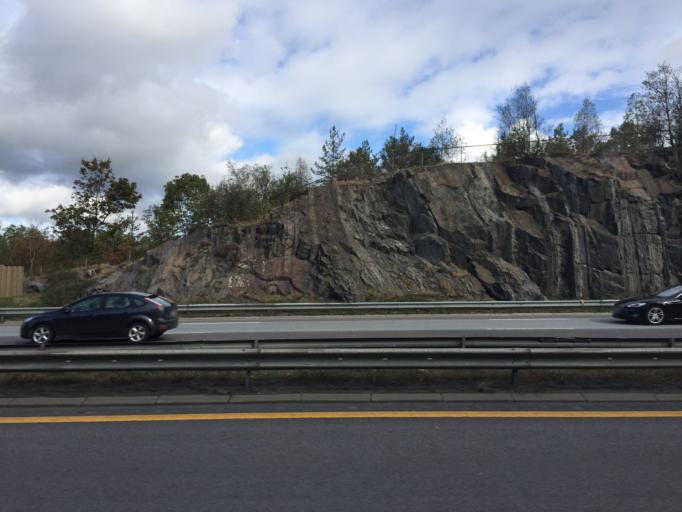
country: NO
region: Akershus
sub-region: Lorenskog
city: Kjenn
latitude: 59.9400
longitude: 10.9165
